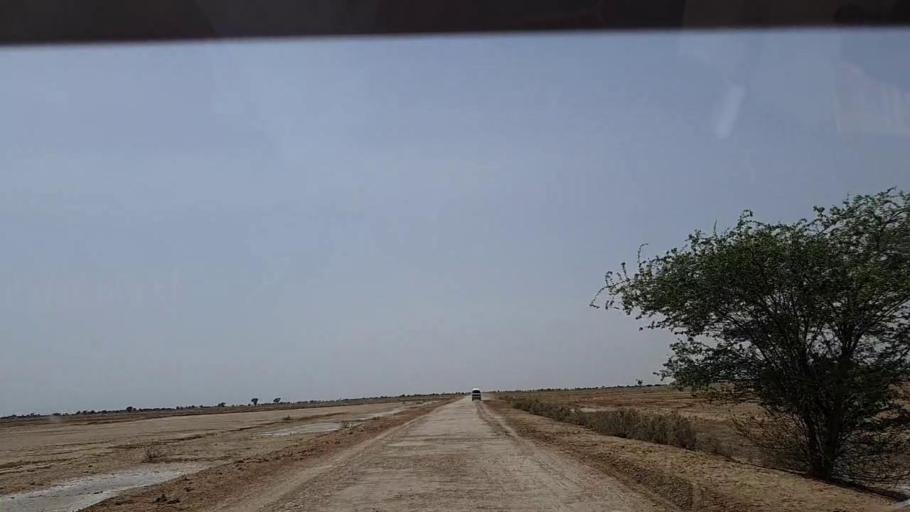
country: PK
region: Sindh
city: Johi
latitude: 26.7419
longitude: 67.6303
